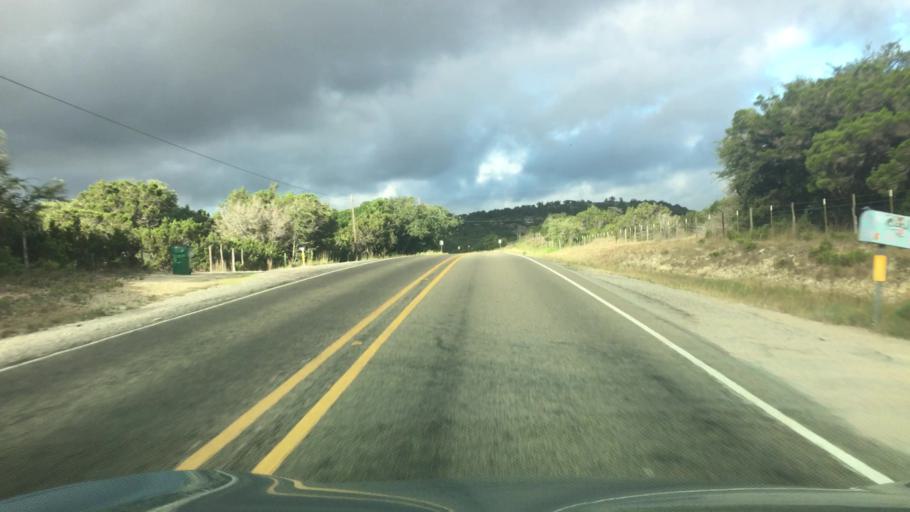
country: US
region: Texas
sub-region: Hays County
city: Dripping Springs
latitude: 30.1566
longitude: -98.2499
